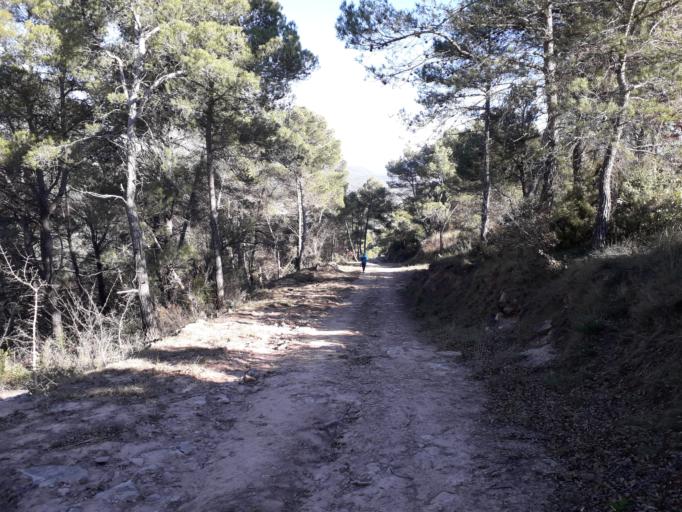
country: ES
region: Catalonia
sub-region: Provincia de Barcelona
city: Sant Marti de Tous
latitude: 41.5959
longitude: 1.4867
